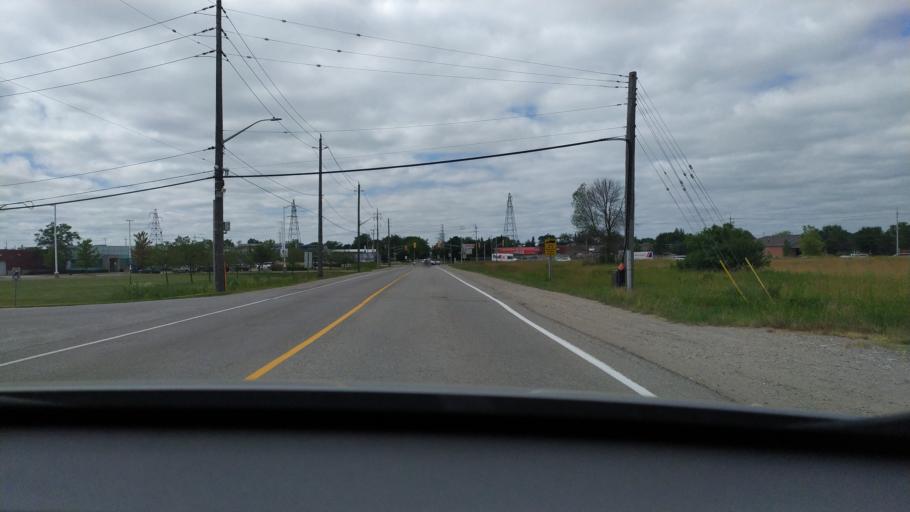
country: CA
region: Ontario
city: Stratford
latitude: 43.3513
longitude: -80.9714
